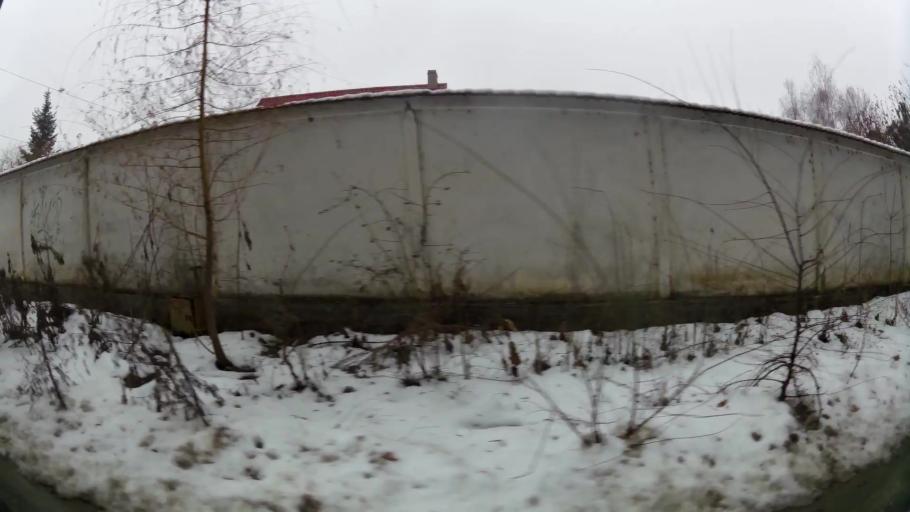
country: RO
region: Ilfov
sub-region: Comuna Chiajna
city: Rosu
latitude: 44.4550
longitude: 26.0036
